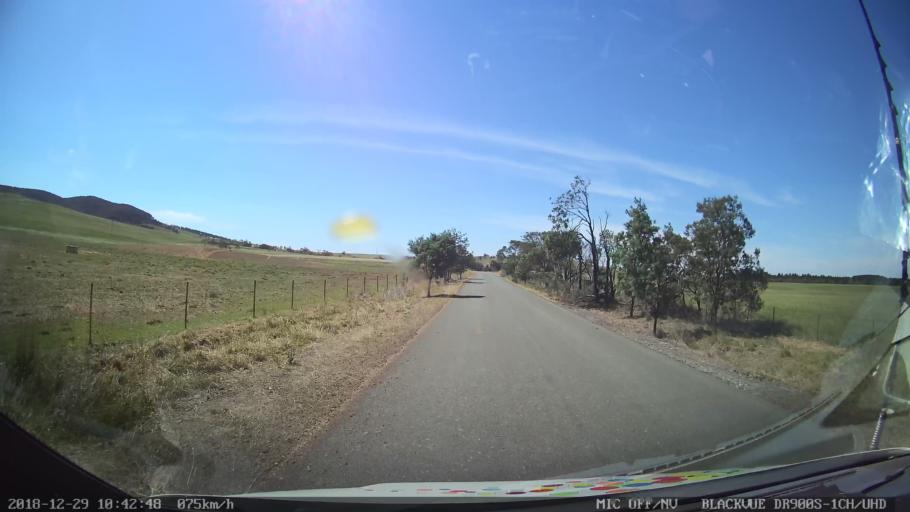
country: AU
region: New South Wales
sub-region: Palerang
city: Bungendore
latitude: -35.0356
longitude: 149.5339
